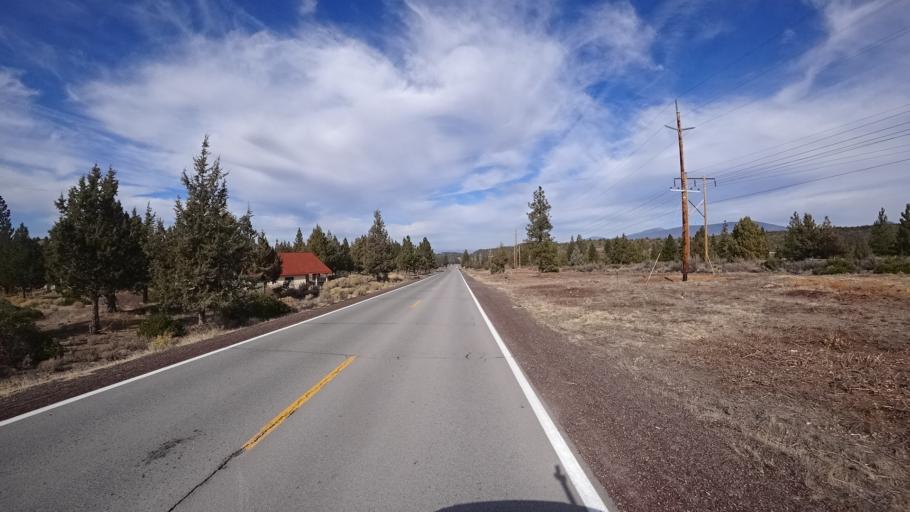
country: US
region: California
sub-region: Siskiyou County
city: Weed
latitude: 41.5018
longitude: -122.3633
